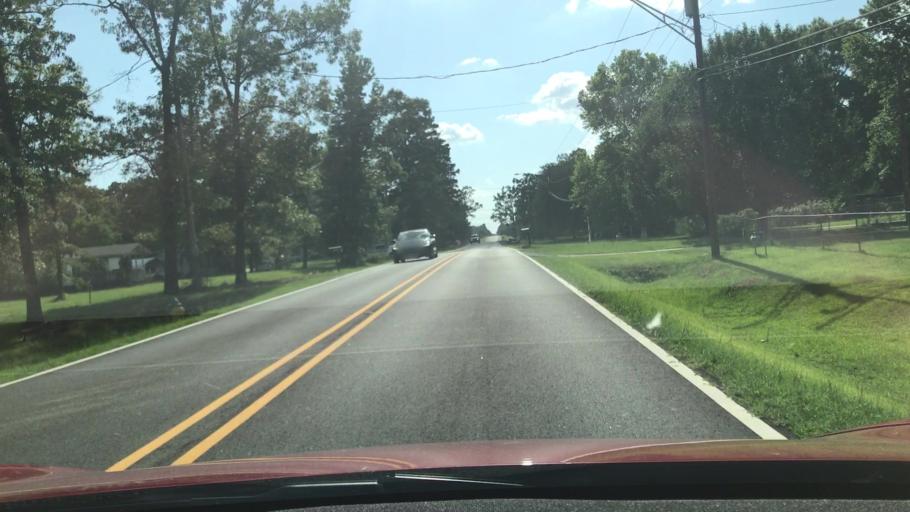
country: US
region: Louisiana
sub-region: Bossier Parish
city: Bossier City
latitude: 32.3909
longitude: -93.7426
